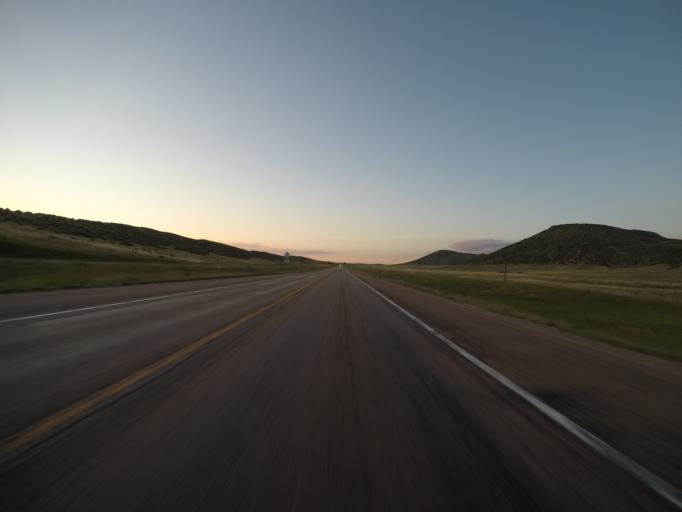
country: US
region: Colorado
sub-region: Larimer County
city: Laporte
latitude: 40.7321
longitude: -105.1712
